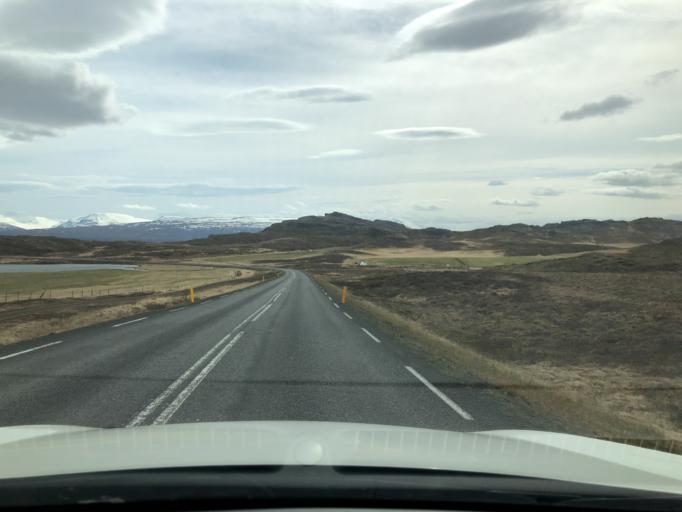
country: IS
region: East
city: Egilsstadir
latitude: 65.3053
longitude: -14.4617
